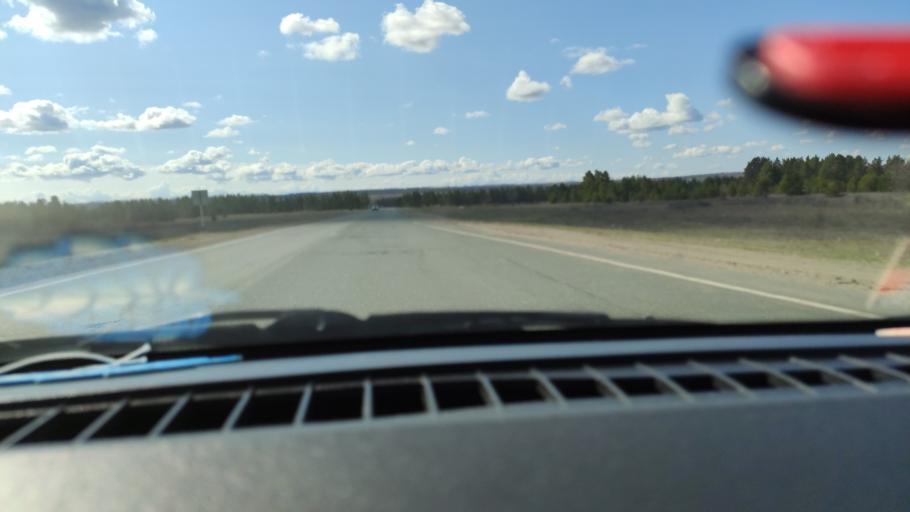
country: RU
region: Samara
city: Varlamovo
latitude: 53.1489
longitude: 48.2842
